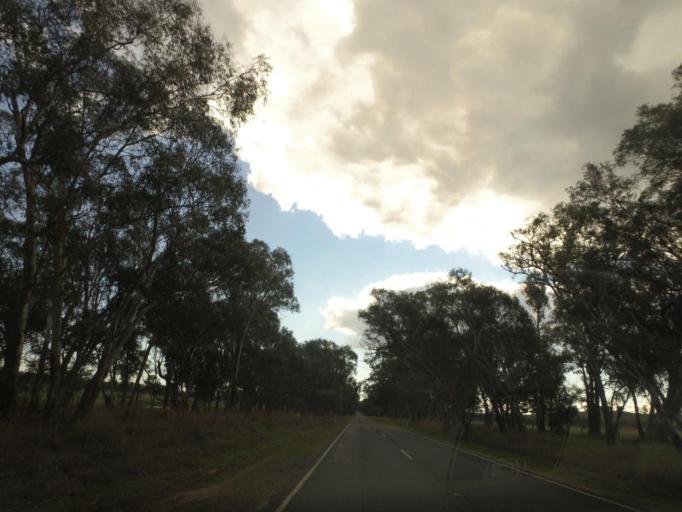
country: AU
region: New South Wales
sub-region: Corowa Shire
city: Howlong
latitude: -36.1924
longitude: 146.6153
